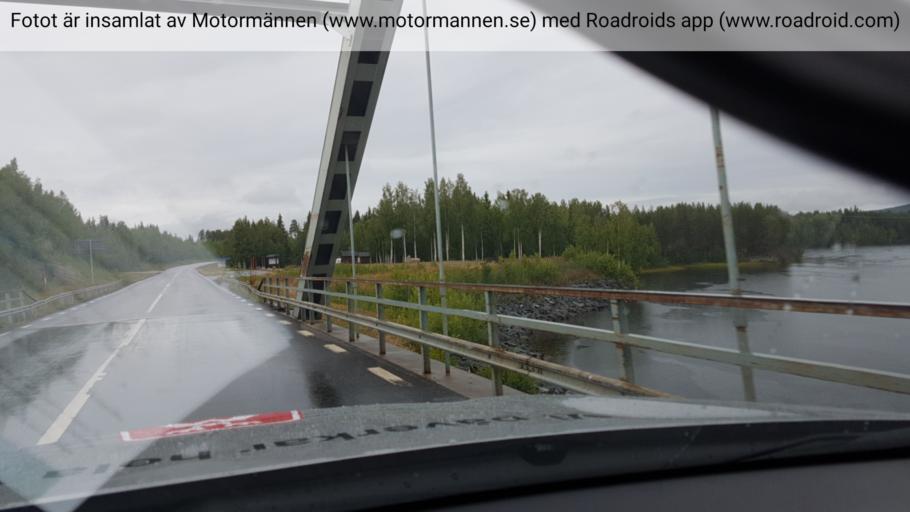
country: SE
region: Norrbotten
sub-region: Alvsbyns Kommun
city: AElvsbyn
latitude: 66.2317
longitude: 20.8706
